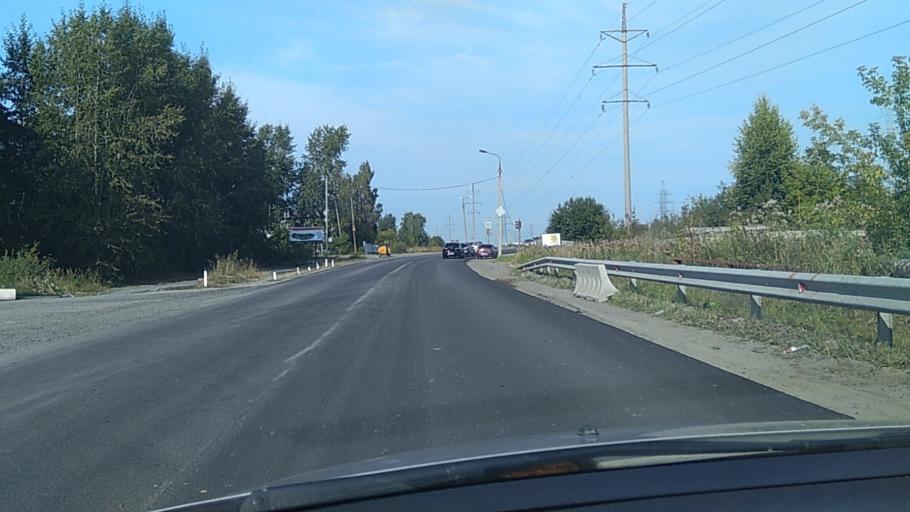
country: RU
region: Sverdlovsk
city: Sredneuralsk
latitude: 56.9831
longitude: 60.4764
